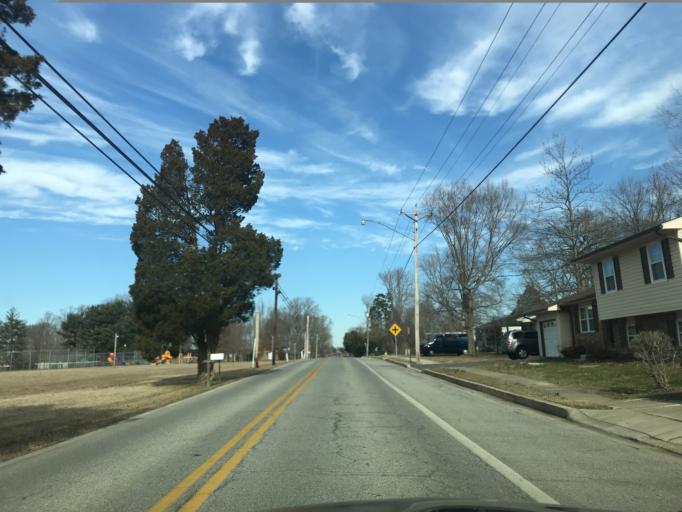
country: US
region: Maryland
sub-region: Charles County
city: La Plata
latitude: 38.5187
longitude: -76.9778
